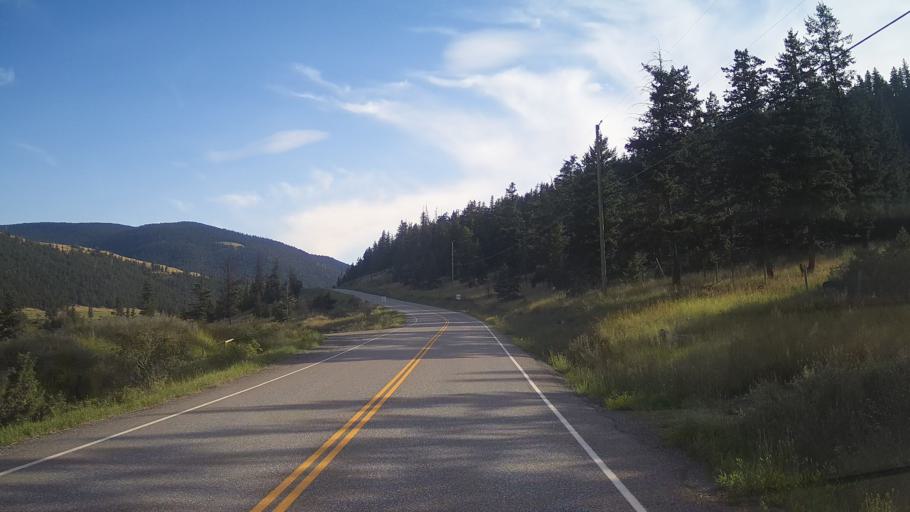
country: CA
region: British Columbia
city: Cache Creek
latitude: 50.8506
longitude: -121.5374
